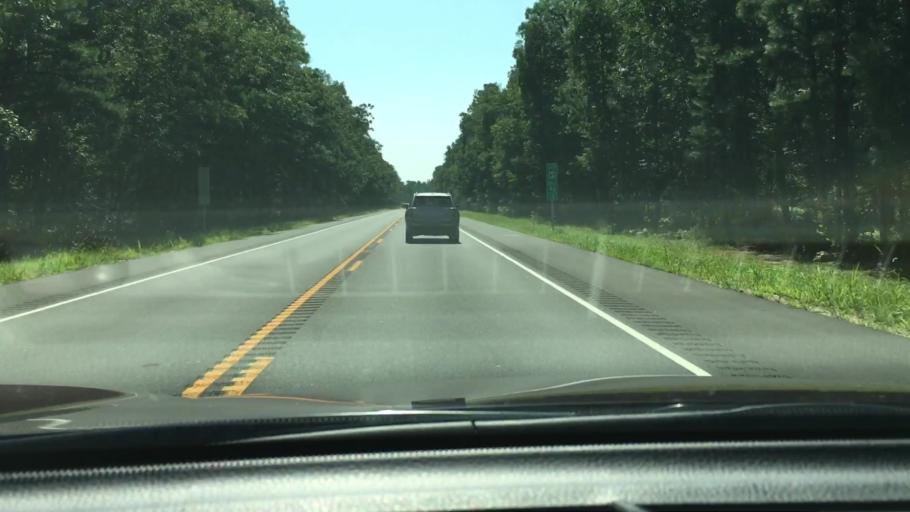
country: US
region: New Jersey
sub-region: Cape May County
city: Woodbine
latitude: 39.3291
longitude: -74.8733
